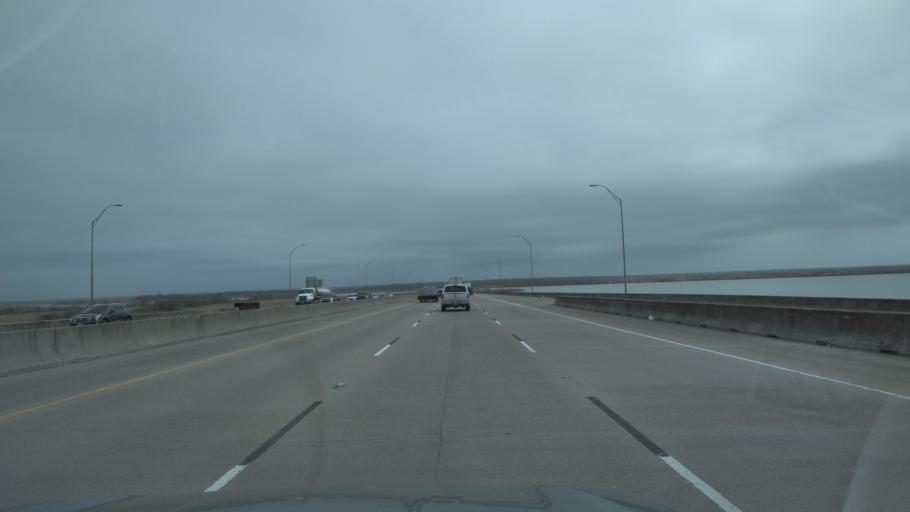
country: US
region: Texas
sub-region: Chambers County
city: Old River-Winfree
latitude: 29.8307
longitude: -94.8024
